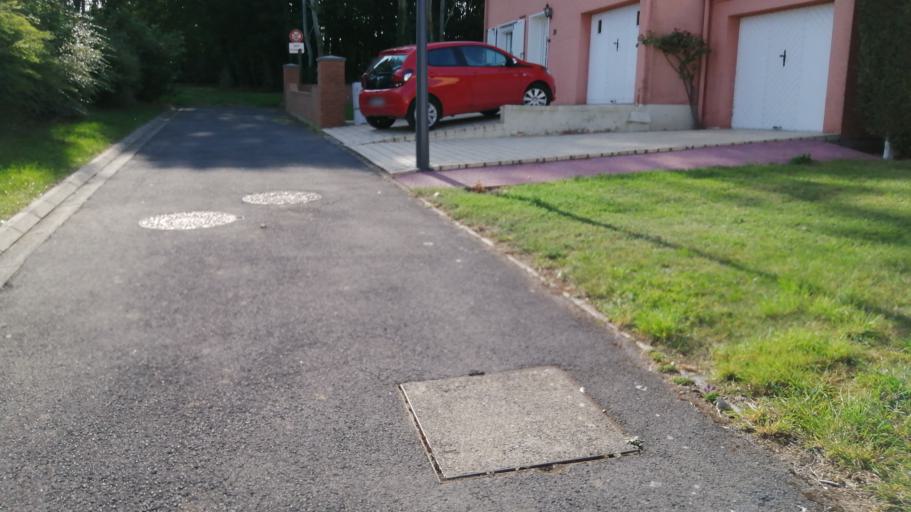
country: FR
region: Nord-Pas-de-Calais
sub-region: Departement du Pas-de-Calais
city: Dainville
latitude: 50.2780
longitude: 2.7230
